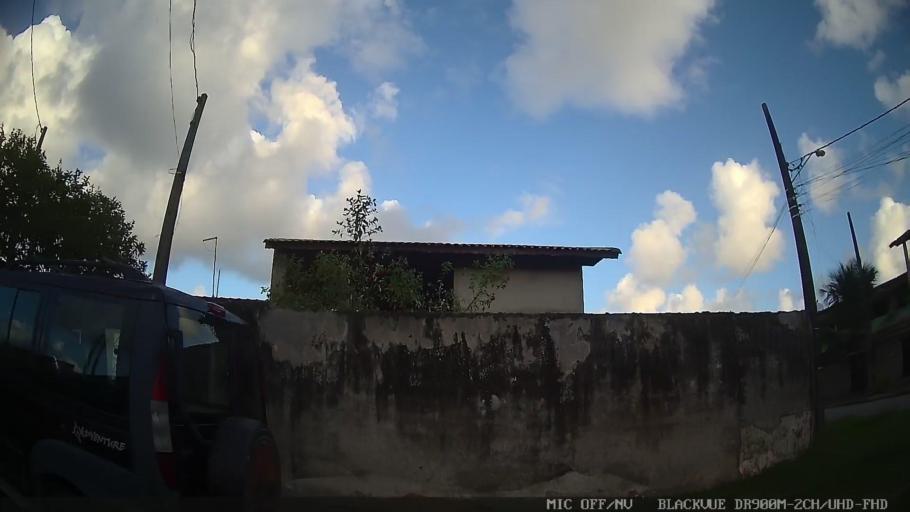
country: BR
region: Sao Paulo
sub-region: Itanhaem
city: Itanhaem
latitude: -24.1442
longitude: -46.7250
